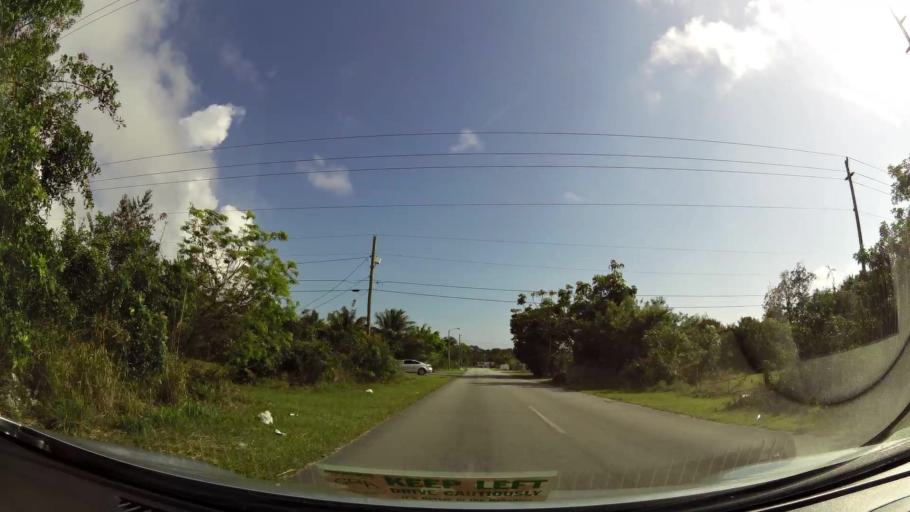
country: BS
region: Freeport
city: Lucaya
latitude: 26.5241
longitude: -78.6763
